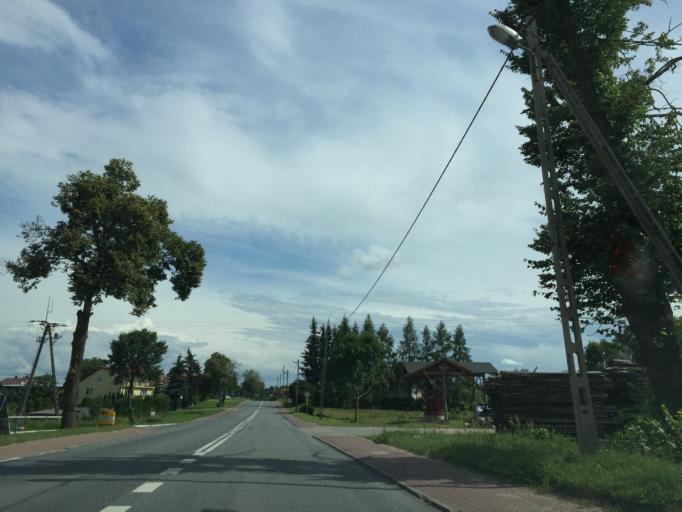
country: PL
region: Masovian Voivodeship
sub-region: Powiat losicki
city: Sarnaki
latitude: 52.3198
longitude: 22.8833
